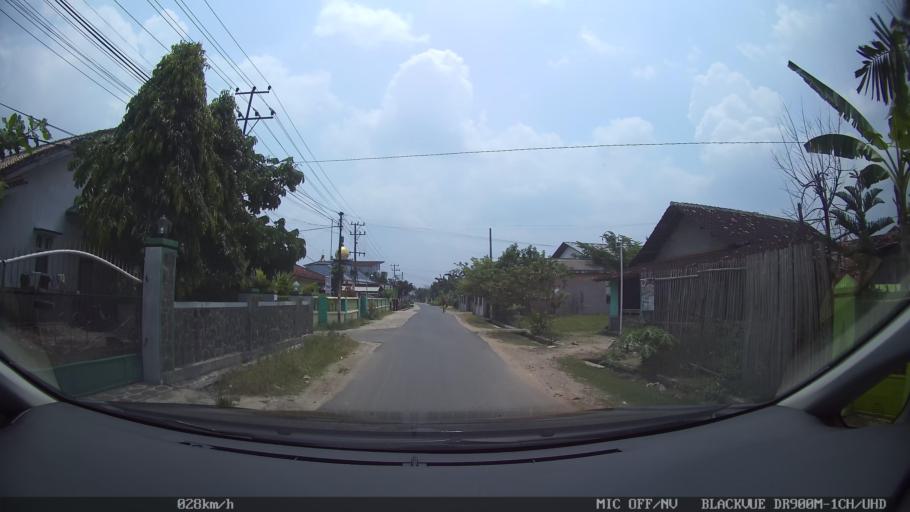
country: ID
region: Lampung
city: Pringsewu
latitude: -5.3509
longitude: 104.9659
